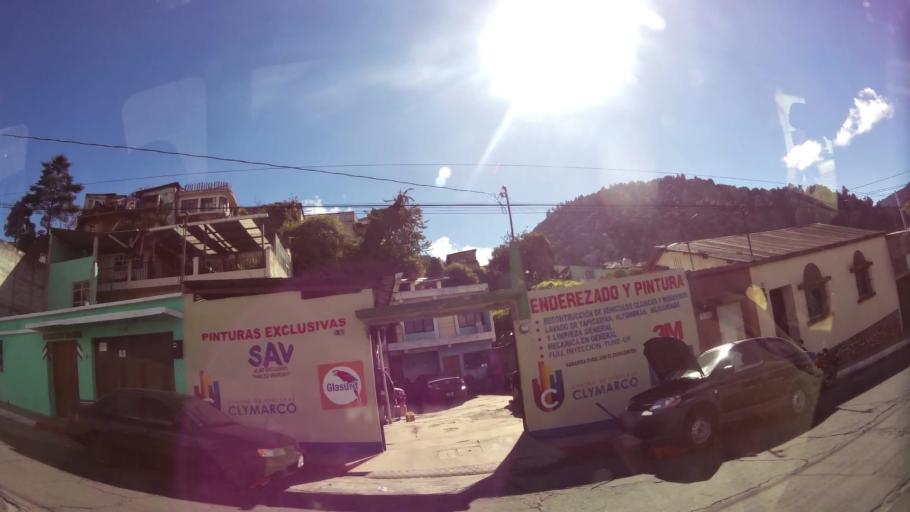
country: GT
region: Quetzaltenango
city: Quetzaltenango
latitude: 14.8357
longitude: -91.5080
